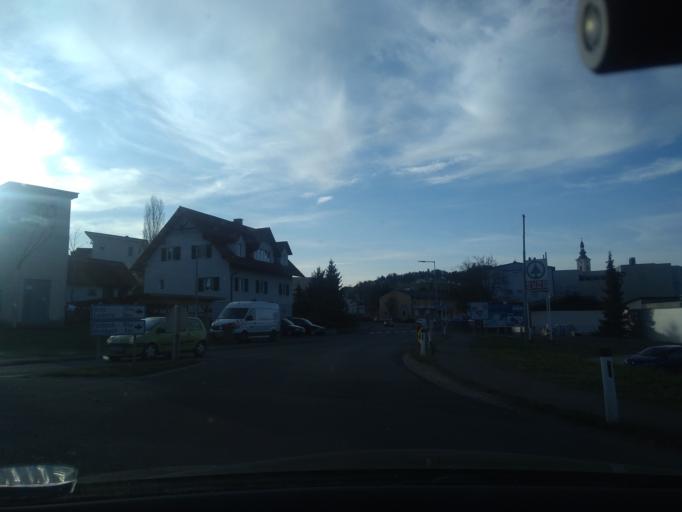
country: AT
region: Styria
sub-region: Politischer Bezirk Suedoststeiermark
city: Sankt Stefan im Rosental
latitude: 46.9016
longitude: 15.7131
